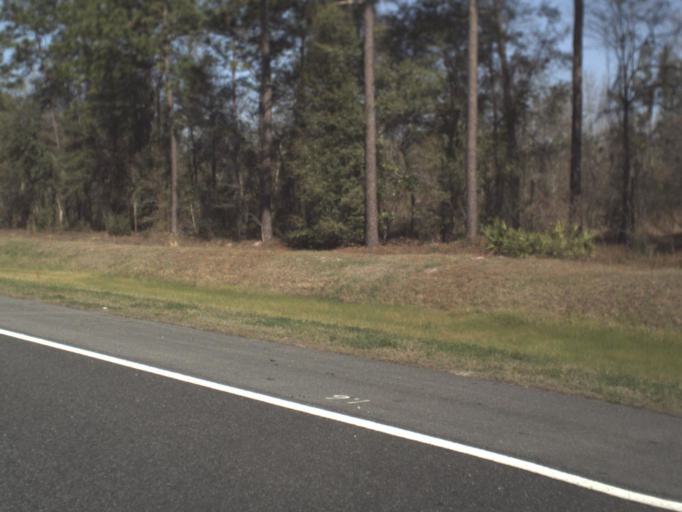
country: US
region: Florida
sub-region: Gadsden County
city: Midway
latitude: 30.4817
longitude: -84.3721
